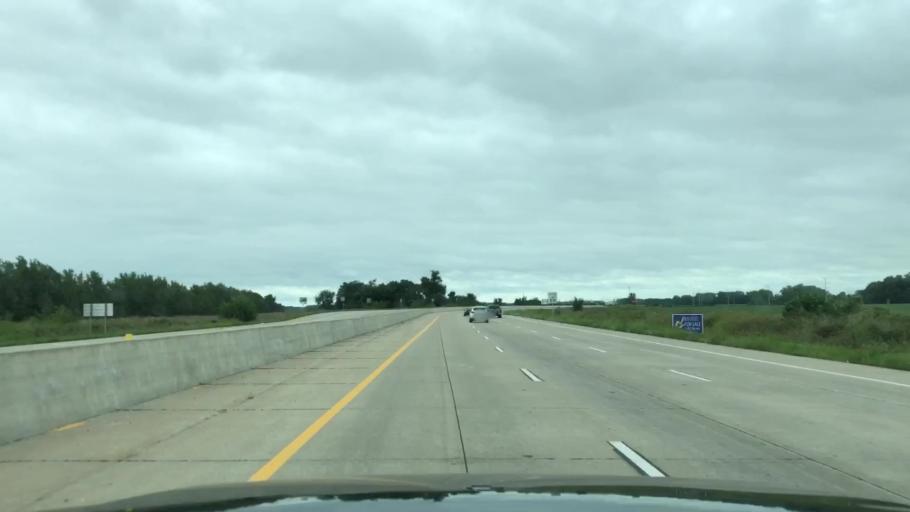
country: US
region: Missouri
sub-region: Saint Louis County
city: Maryland Heights
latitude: 38.7102
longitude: -90.5016
